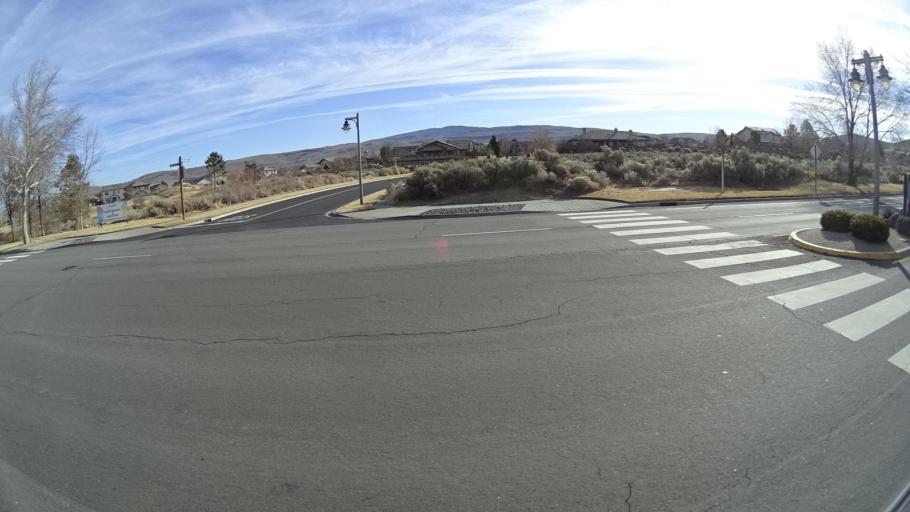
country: US
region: Nevada
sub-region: Washoe County
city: Spanish Springs
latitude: 39.6085
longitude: -119.6868
